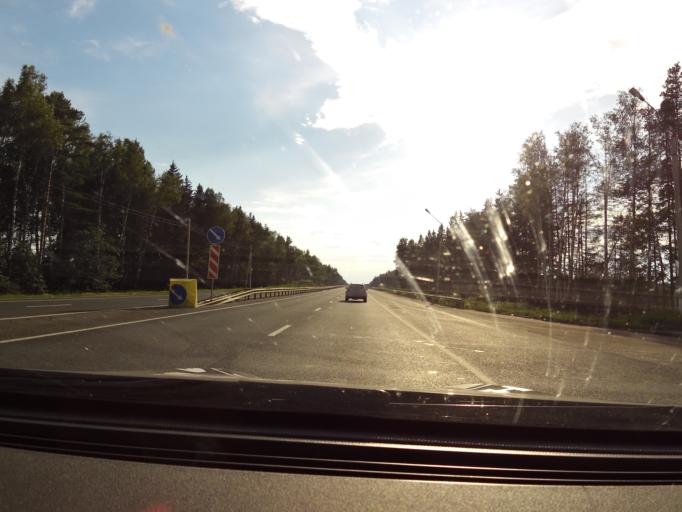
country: RU
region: Vladimir
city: Krasnyy Oktyabr'
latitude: 56.2190
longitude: 41.4719
